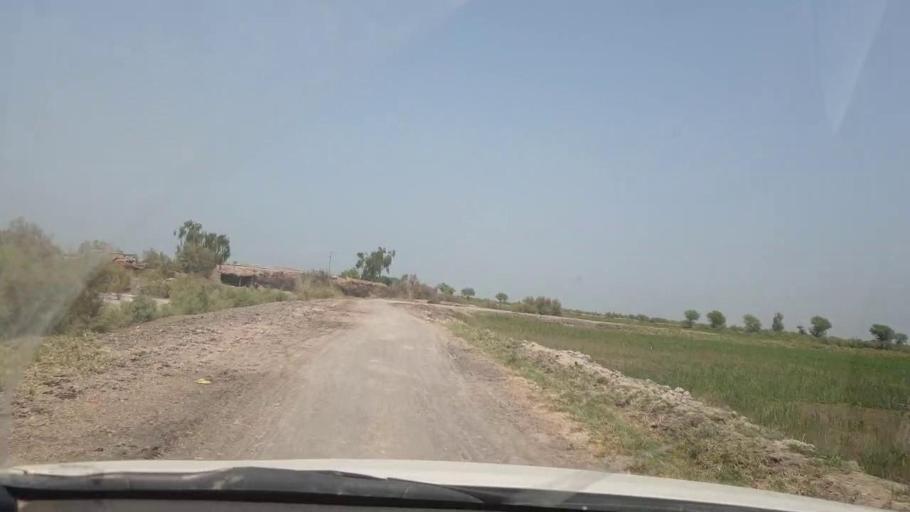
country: PK
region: Sindh
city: Lakhi
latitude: 27.8838
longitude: 68.7403
